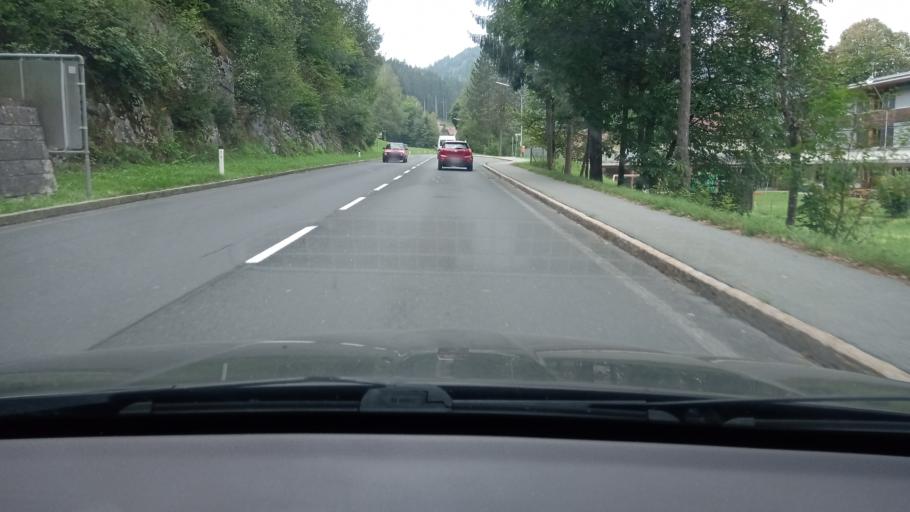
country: AT
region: Carinthia
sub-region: Politischer Bezirk Hermagor
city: Hermagor
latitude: 46.6261
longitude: 13.3684
